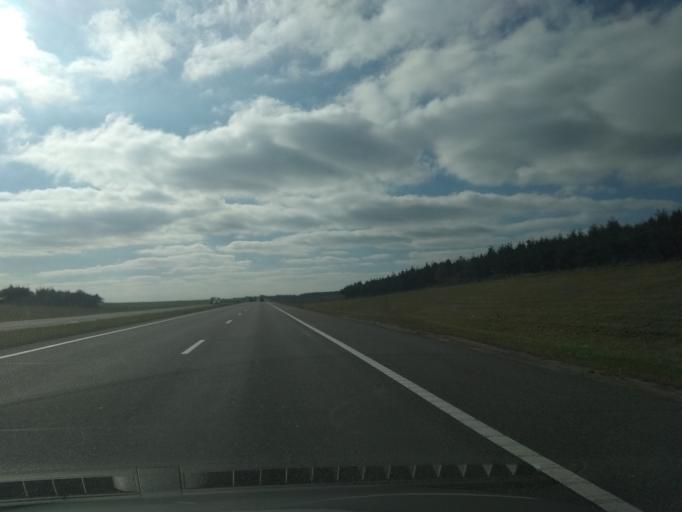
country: BY
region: Grodnenskaya
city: Mir
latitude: 53.4366
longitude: 26.5882
